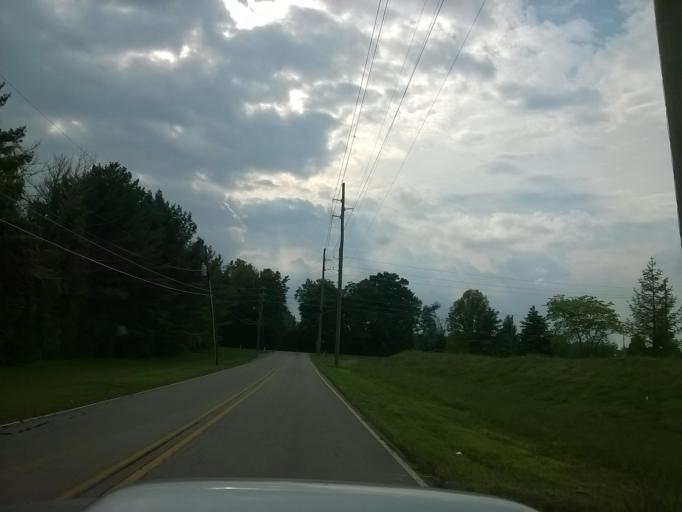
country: US
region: Indiana
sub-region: Hamilton County
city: Carmel
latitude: 39.9489
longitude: -86.1635
